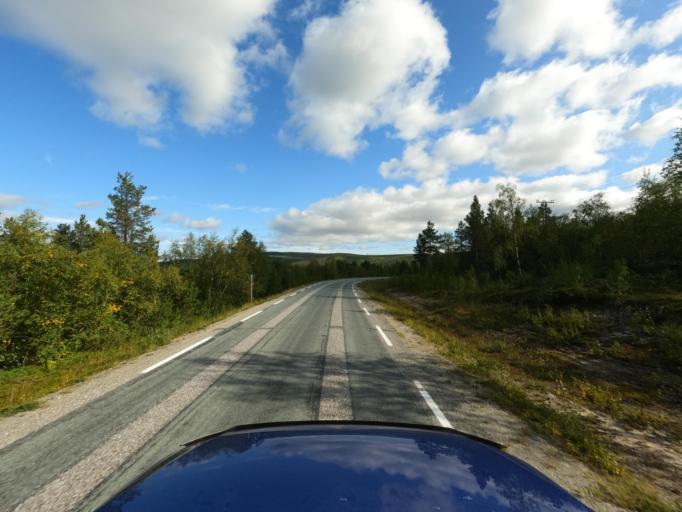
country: NO
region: Finnmark Fylke
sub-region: Karasjok
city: Karasjohka
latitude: 69.4295
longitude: 25.7860
